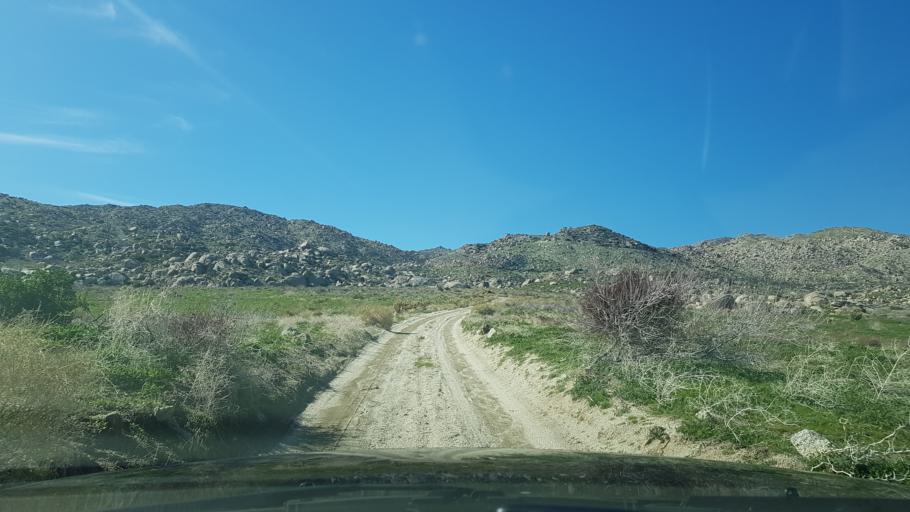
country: US
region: California
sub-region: San Diego County
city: Borrego Springs
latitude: 33.2097
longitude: -116.4547
